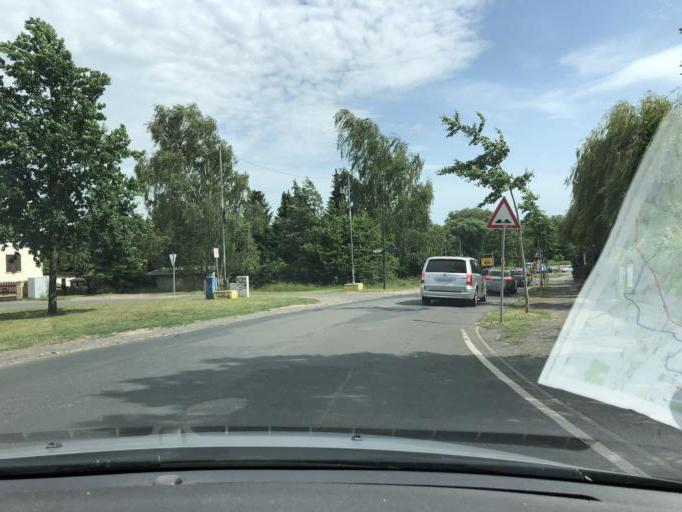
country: DE
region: Saxony
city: Taucha
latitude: 51.3834
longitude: 12.4928
